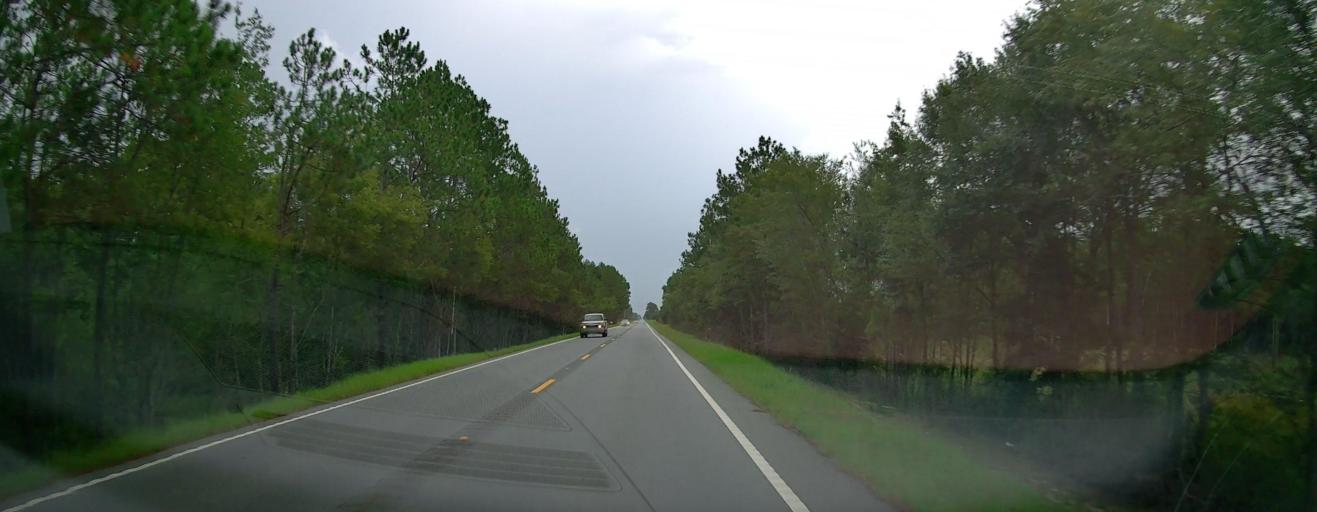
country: US
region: Georgia
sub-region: Brantley County
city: Nahunta
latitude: 31.3474
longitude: -82.0157
